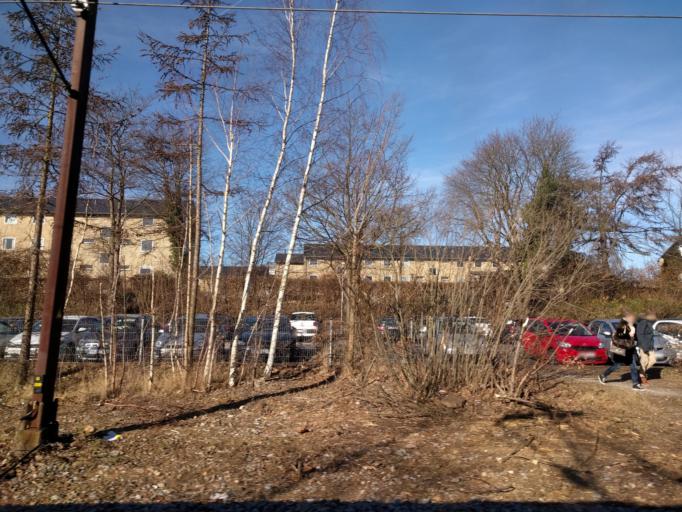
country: DK
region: Capital Region
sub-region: Helsingor Kommune
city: Espergaerde
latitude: 55.9941
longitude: 12.5480
